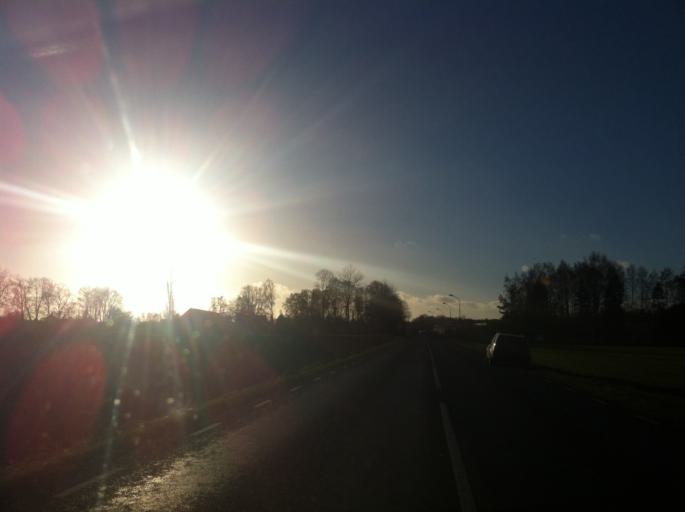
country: SE
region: Skane
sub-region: Ostra Goinge Kommun
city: Sibbhult
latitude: 56.2034
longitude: 14.1693
